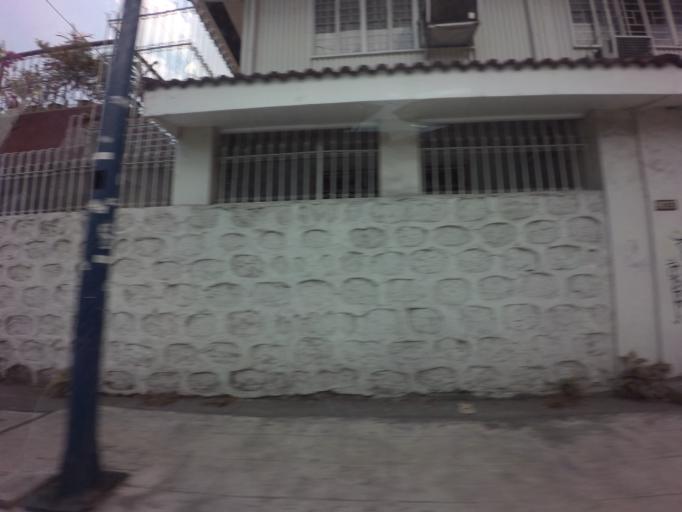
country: PH
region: Metro Manila
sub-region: Mandaluyong
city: Mandaluyong City
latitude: 14.5706
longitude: 121.0260
